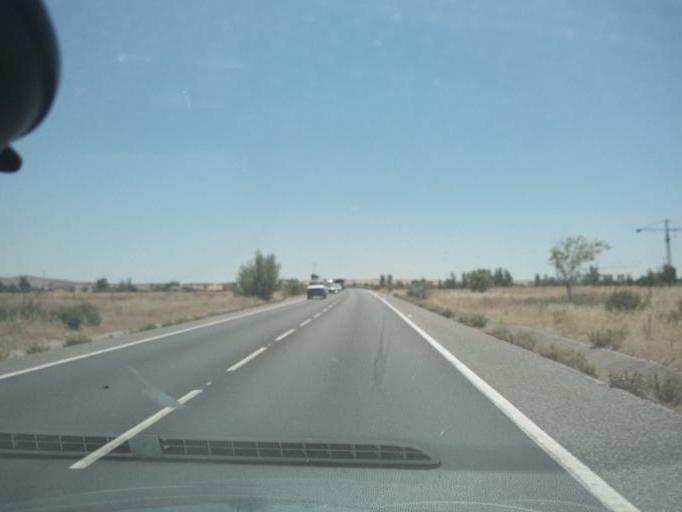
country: ES
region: Madrid
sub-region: Provincia de Madrid
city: Cobena
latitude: 40.5809
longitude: -3.5457
